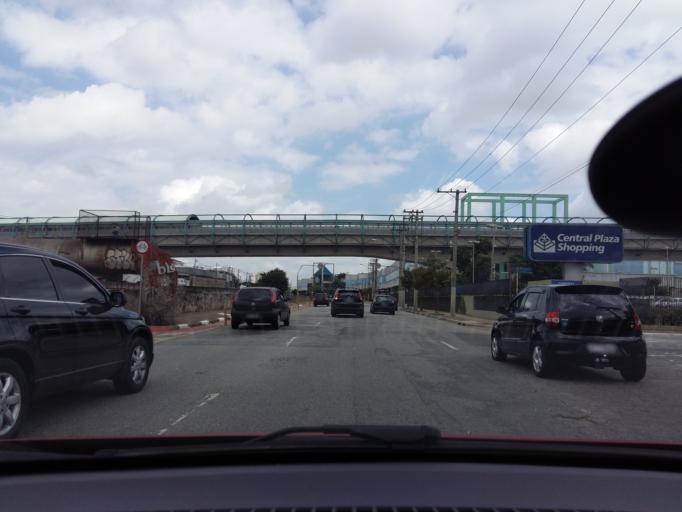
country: BR
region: Sao Paulo
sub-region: Sao Caetano Do Sul
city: Sao Caetano do Sul
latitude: -23.5903
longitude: -46.5881
